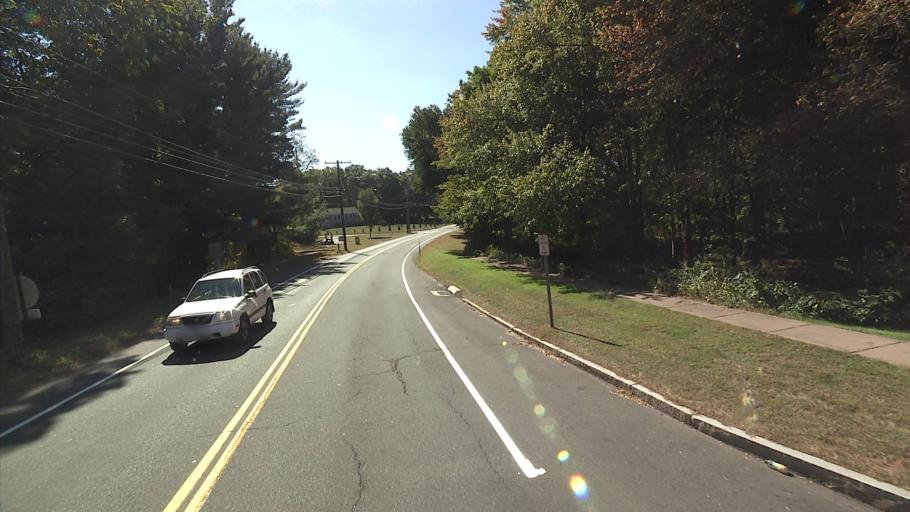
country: US
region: Connecticut
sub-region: Hartford County
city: Manchester
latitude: 41.7409
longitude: -72.5171
